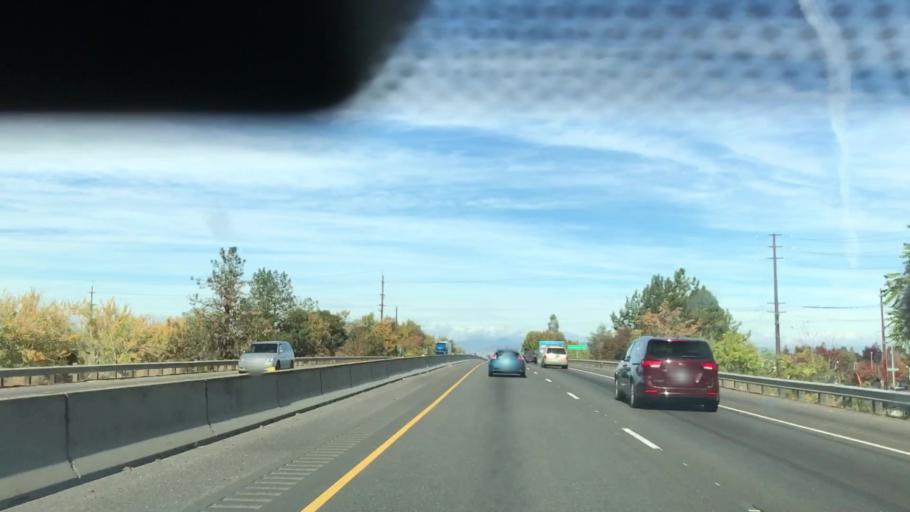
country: US
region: Oregon
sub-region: Jackson County
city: Medford
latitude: 42.3397
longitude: -122.8730
